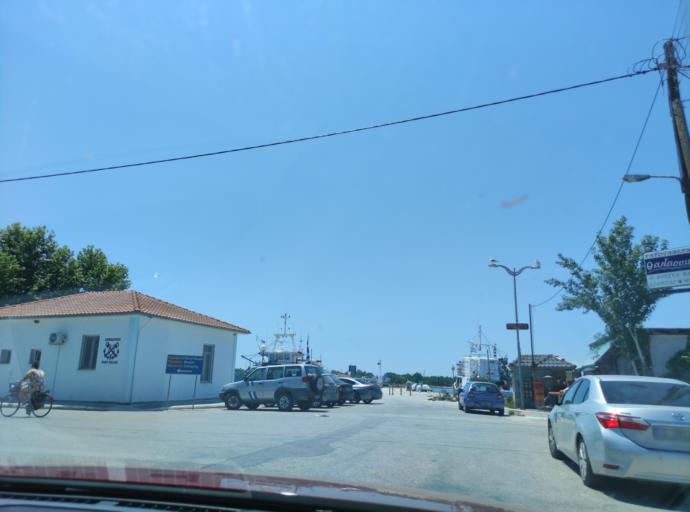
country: GR
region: East Macedonia and Thrace
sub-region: Nomos Kavalas
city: Keramoti
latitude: 40.8591
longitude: 24.7038
